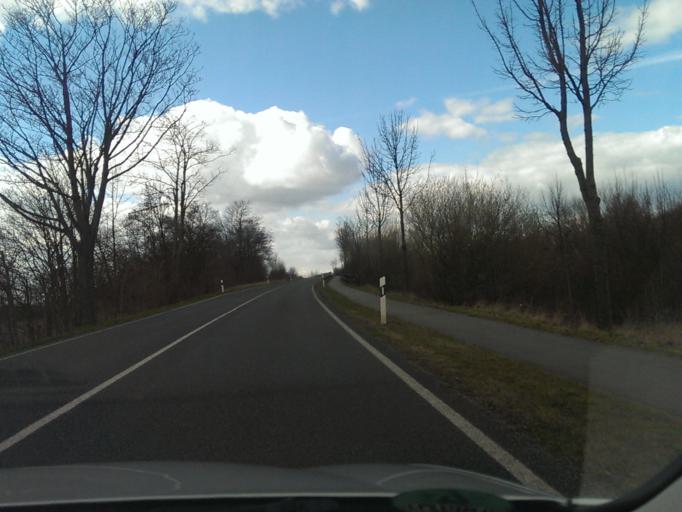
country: DE
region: Lower Saxony
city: Dollbergen
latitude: 52.3589
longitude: 10.1546
